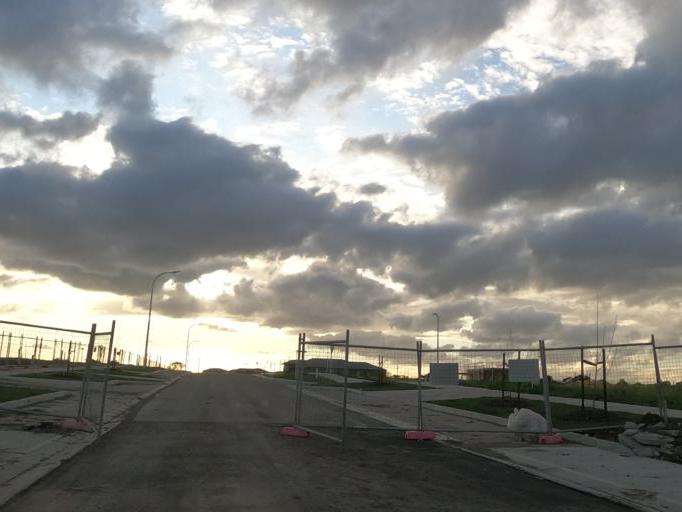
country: AU
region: Victoria
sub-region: Hume
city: Greenvale
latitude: -37.6301
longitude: 144.8894
